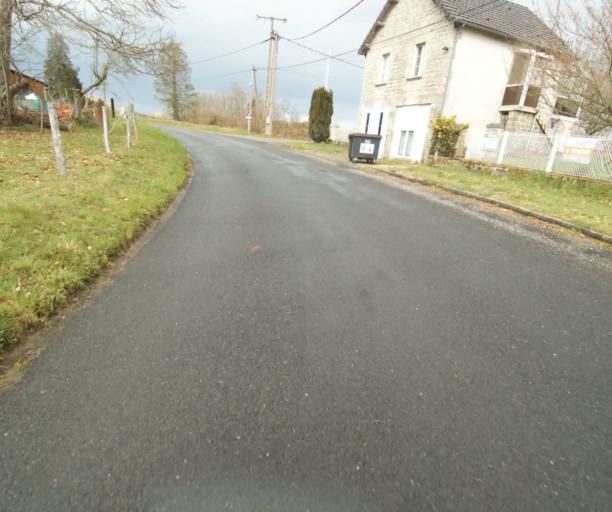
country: FR
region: Limousin
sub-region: Departement de la Correze
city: Egletons
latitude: 45.2576
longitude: 1.9910
